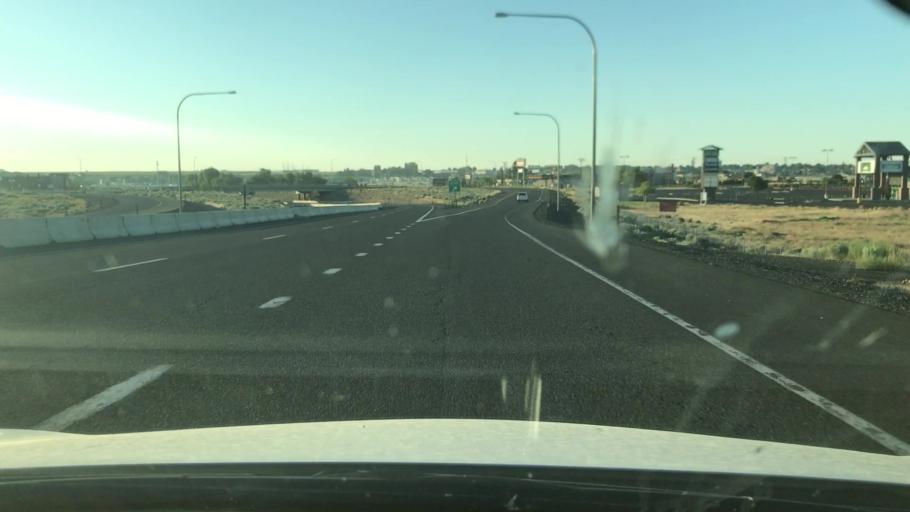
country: US
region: Washington
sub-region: Grant County
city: Moses Lake
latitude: 47.1447
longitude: -119.2832
